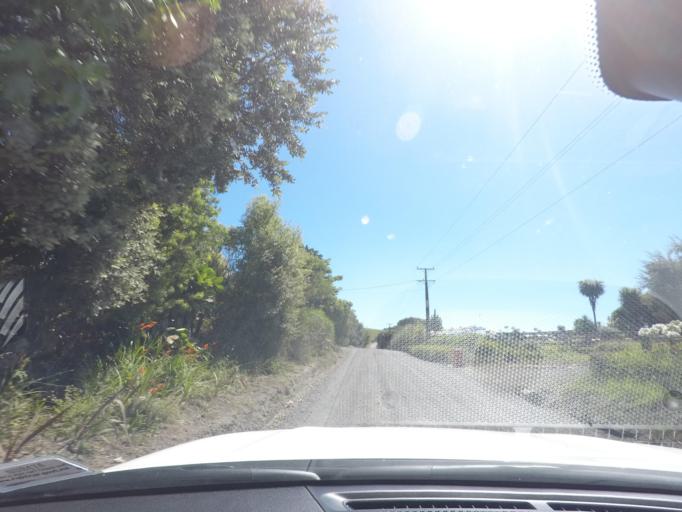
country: NZ
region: Auckland
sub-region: Auckland
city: Parakai
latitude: -36.5811
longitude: 174.3160
